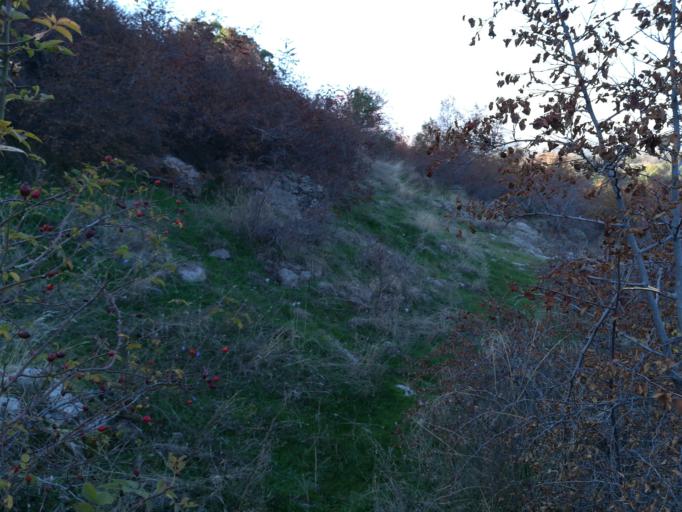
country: BG
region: Khaskovo
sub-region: Obshtina Mineralni Bani
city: Mineralni Bani
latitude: 41.9814
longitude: 25.2385
